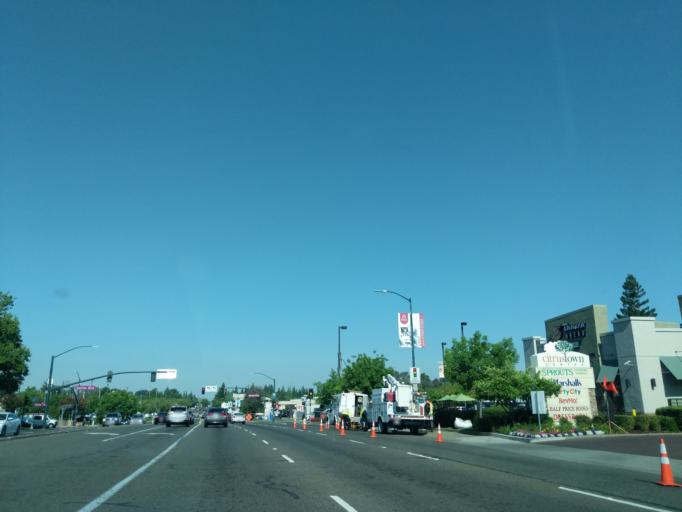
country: US
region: California
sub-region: Sacramento County
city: Citrus Heights
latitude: 38.6785
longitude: -121.2703
